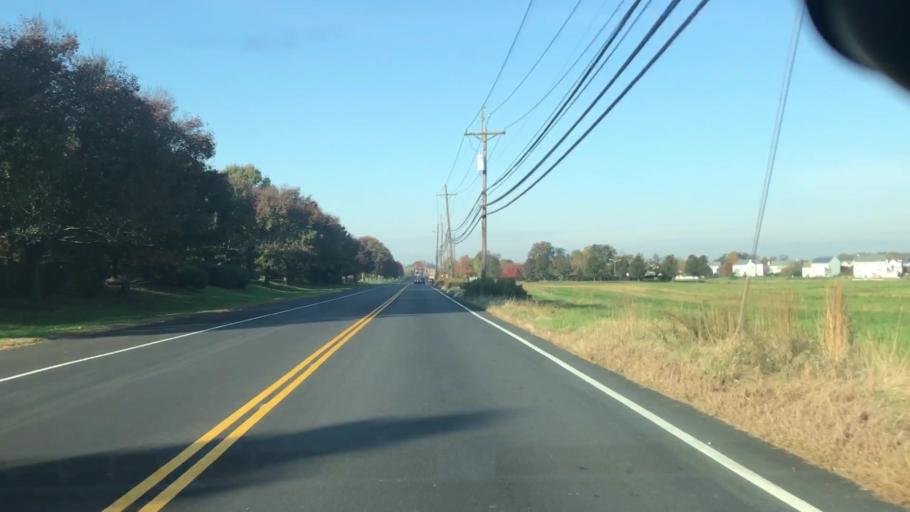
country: US
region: New Jersey
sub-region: Middlesex County
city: Princeton Meadows
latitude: 40.3359
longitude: -74.5787
